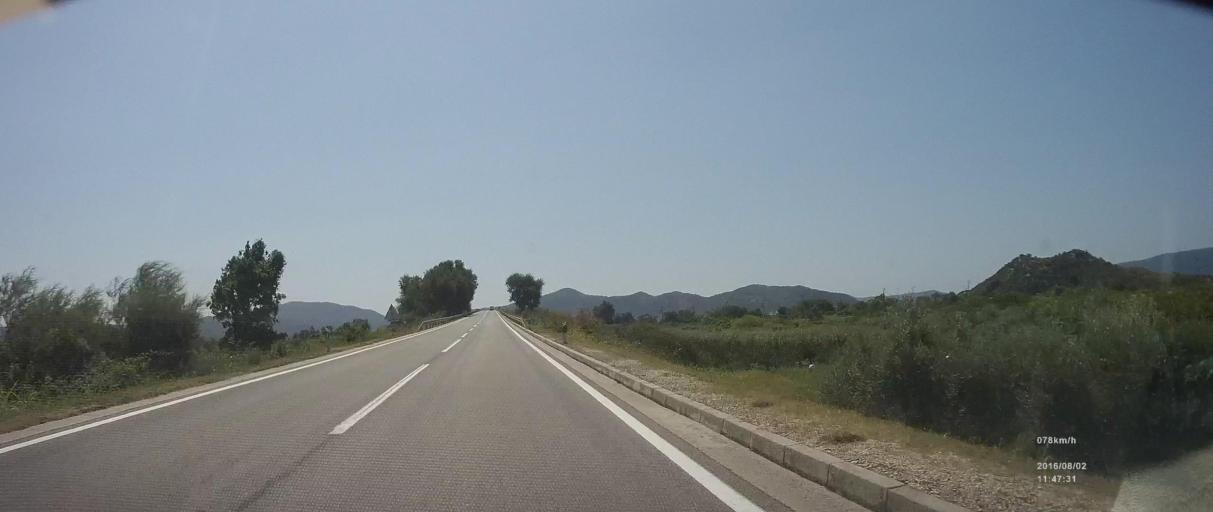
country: HR
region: Dubrovacko-Neretvanska
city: Komin
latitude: 43.0430
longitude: 17.4826
